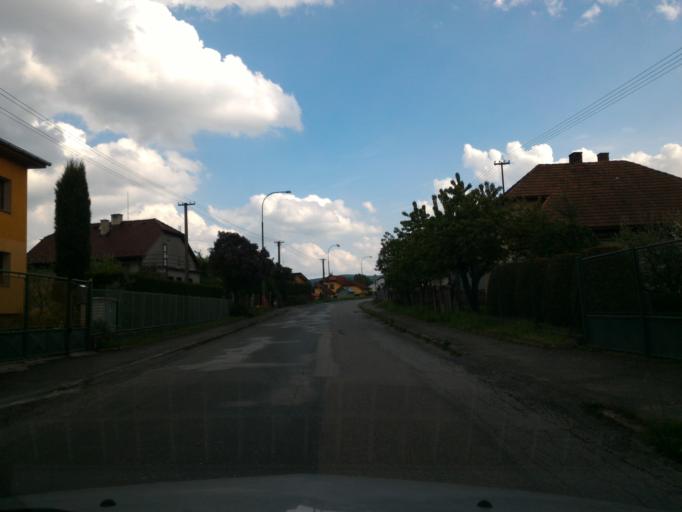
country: CZ
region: Vysocina
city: Ledec nad Sazavou
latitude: 49.6882
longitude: 15.2831
